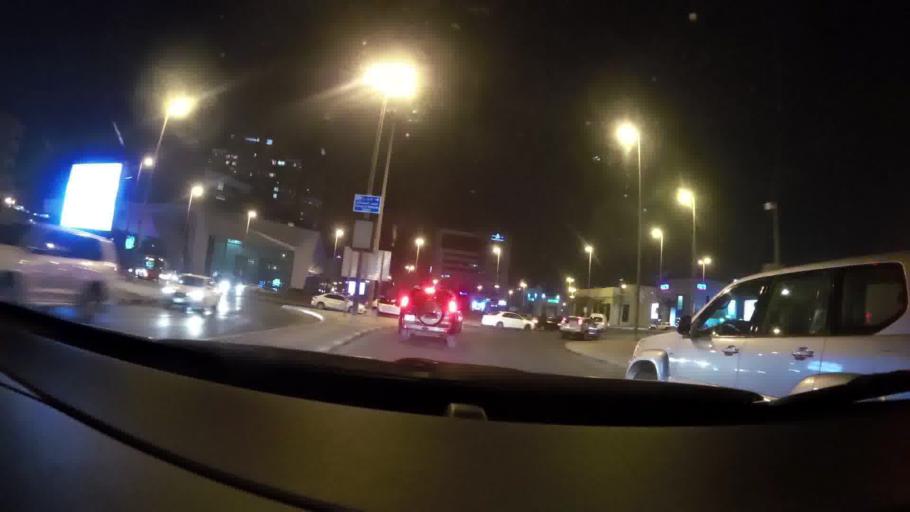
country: KW
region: Muhafazat Hawalli
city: As Salimiyah
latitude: 29.3413
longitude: 48.0831
